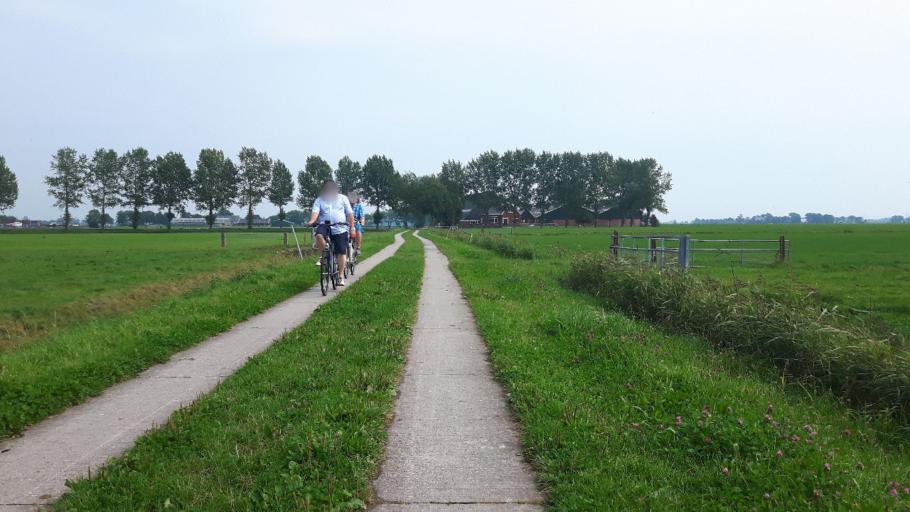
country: NL
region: Groningen
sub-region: Gemeente Winsum
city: Winsum
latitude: 53.3319
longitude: 6.5416
